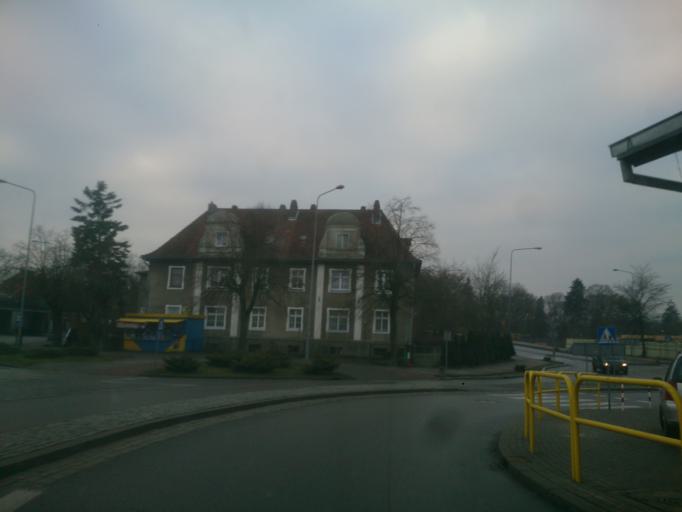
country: PL
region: Pomeranian Voivodeship
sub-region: Powiat bytowski
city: Bytow
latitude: 54.1640
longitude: 17.4881
